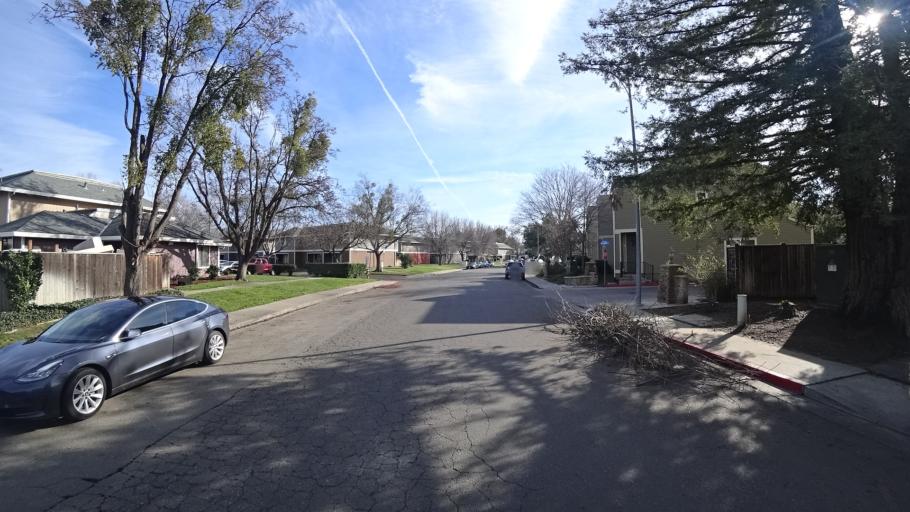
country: US
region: California
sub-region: Yolo County
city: Davis
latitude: 38.5495
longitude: -121.7000
